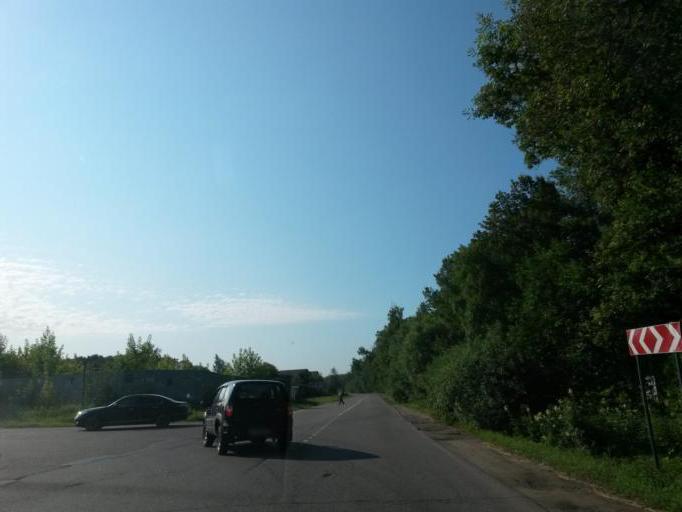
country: RU
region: Moskovskaya
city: Gorki-Leninskiye
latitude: 55.5097
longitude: 37.8081
